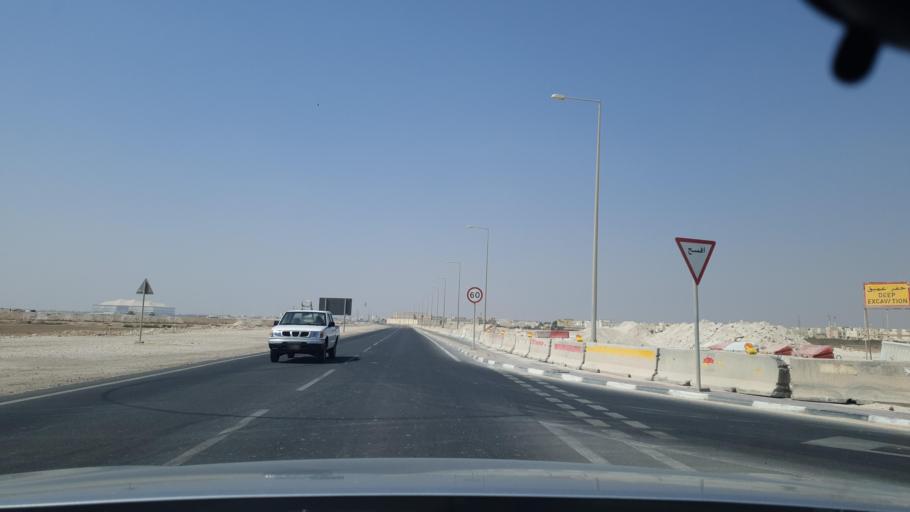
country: QA
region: Al Khawr
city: Al Khawr
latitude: 25.6679
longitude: 51.5255
